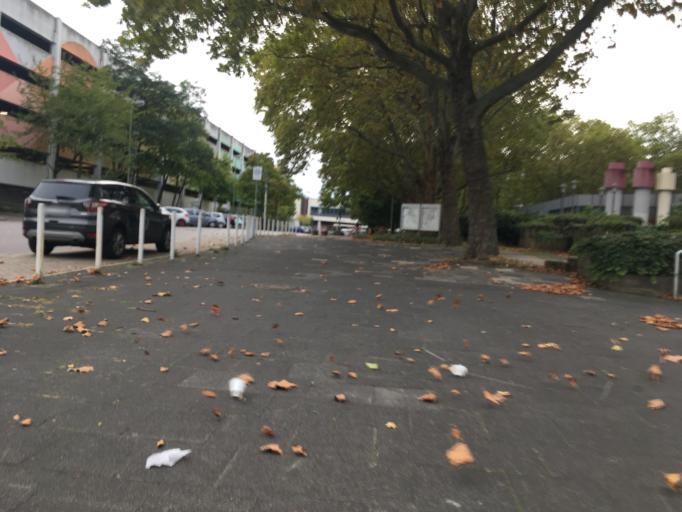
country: DE
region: North Rhine-Westphalia
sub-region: Regierungsbezirk Dusseldorf
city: Essen
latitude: 51.4638
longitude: 7.0092
